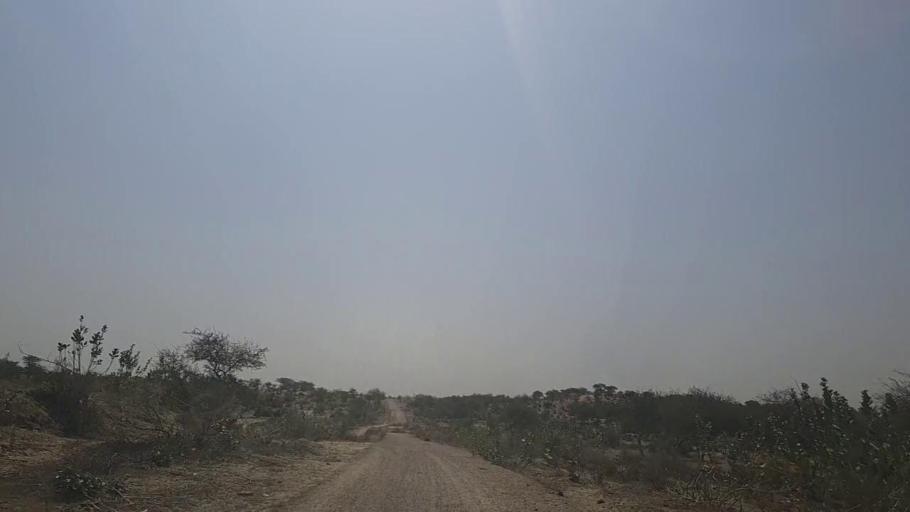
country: PK
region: Sindh
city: Naukot
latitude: 24.8114
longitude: 69.4743
